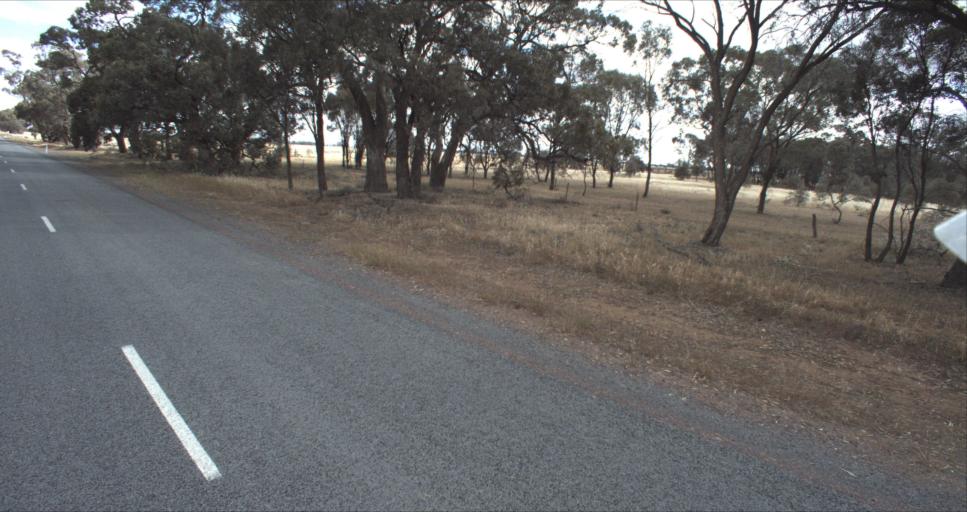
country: AU
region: New South Wales
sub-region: Leeton
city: Leeton
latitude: -34.6665
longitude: 146.3483
